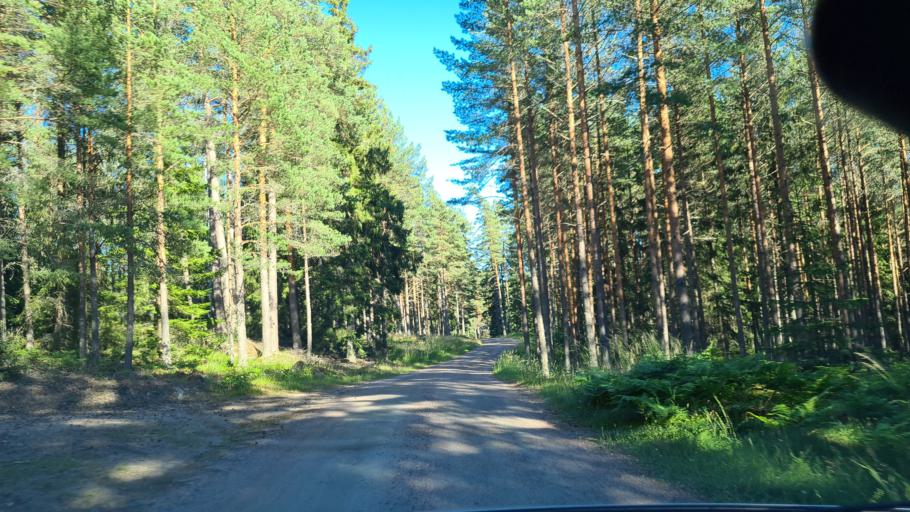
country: SE
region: Soedermanland
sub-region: Nykopings Kommun
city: Nykoping
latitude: 58.9111
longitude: 16.9477
